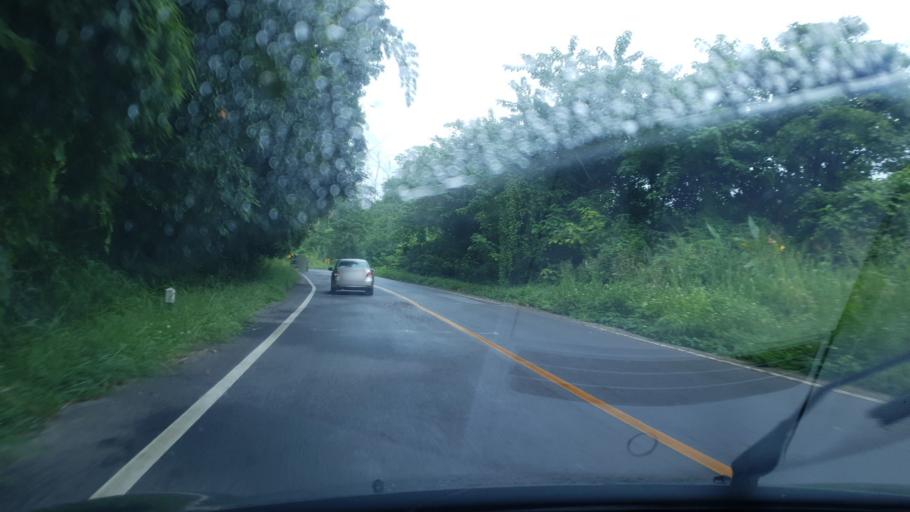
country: TH
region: Mae Hong Son
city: Khun Yuam
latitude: 18.6859
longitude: 97.9196
